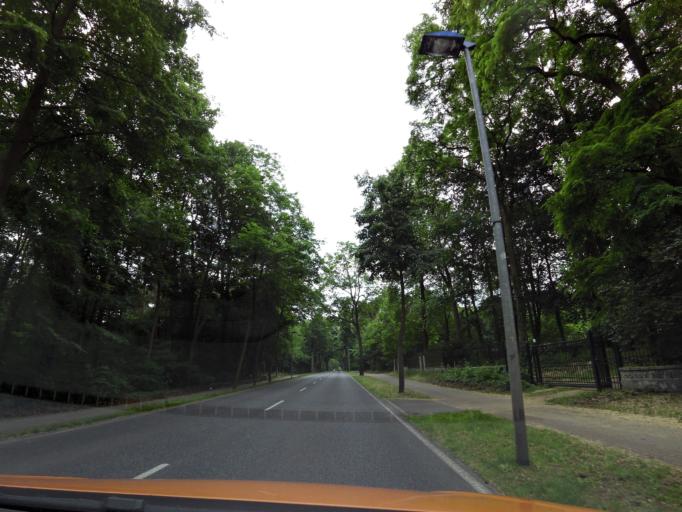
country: DE
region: Brandenburg
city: Zossen
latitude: 52.1606
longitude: 13.4753
